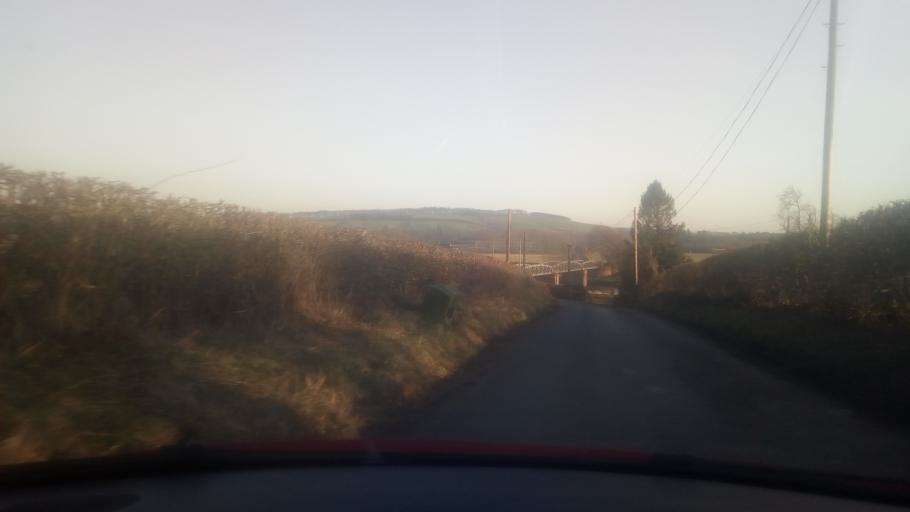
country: GB
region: Scotland
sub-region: The Scottish Borders
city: Jedburgh
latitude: 55.5228
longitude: -2.5183
